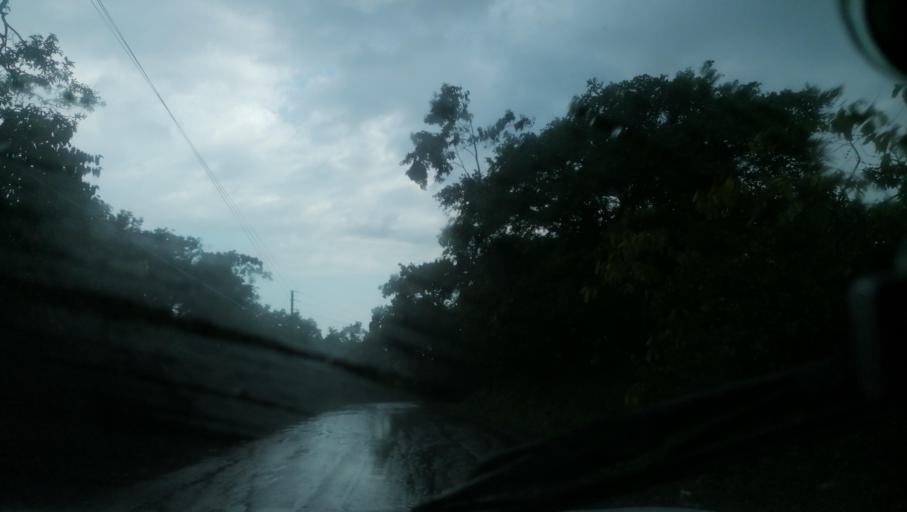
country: MX
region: Chiapas
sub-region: Cacahoatan
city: Benito Juarez
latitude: 15.0652
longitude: -92.1910
